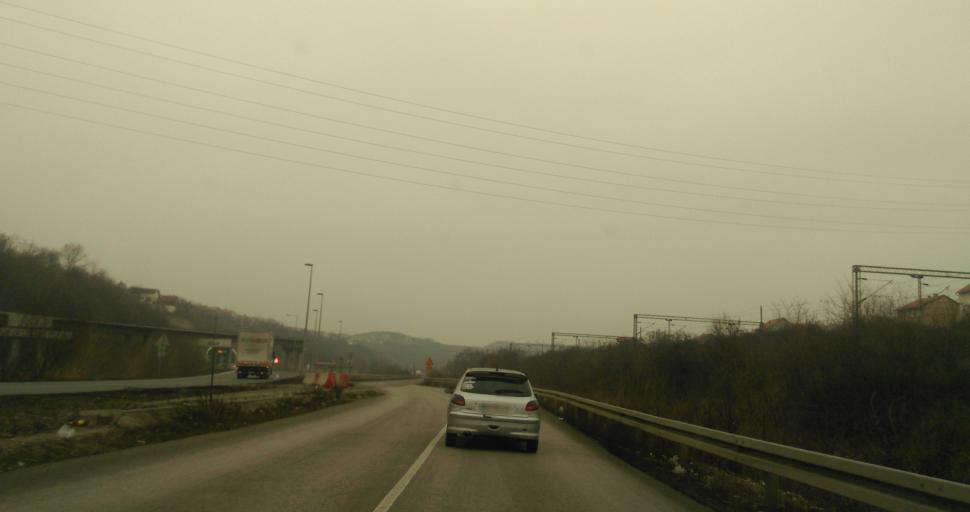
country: RS
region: Central Serbia
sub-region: Belgrade
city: Rakovica
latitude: 44.7195
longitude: 20.4613
